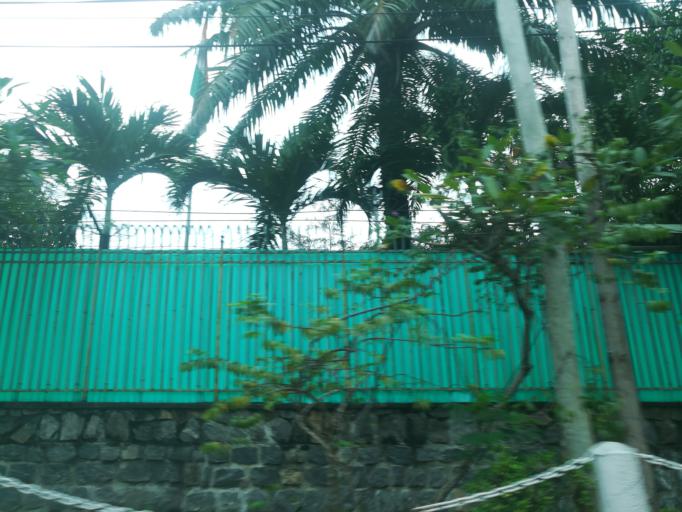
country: NG
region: Lagos
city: Lagos
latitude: 6.4394
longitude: 3.4106
